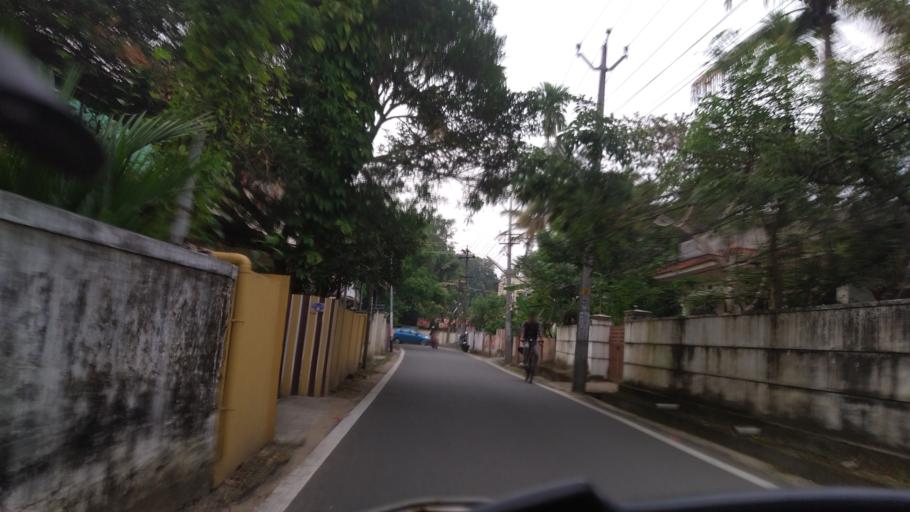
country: IN
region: Kerala
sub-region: Thrissur District
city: Kodungallur
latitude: 10.1386
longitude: 76.2246
